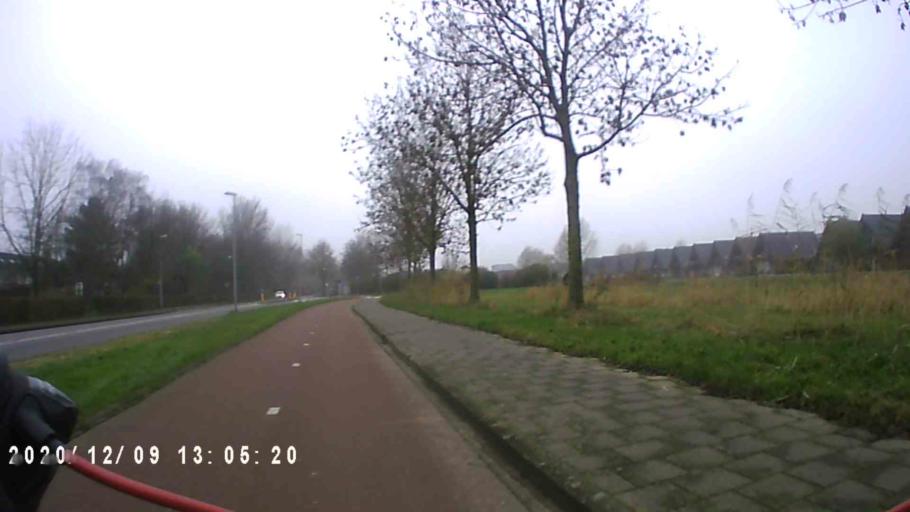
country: NL
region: Groningen
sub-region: Gemeente Groningen
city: Oosterpark
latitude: 53.2421
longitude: 6.6227
